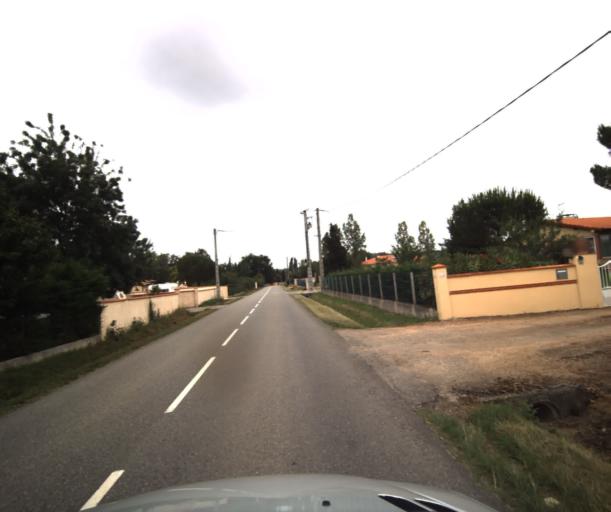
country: FR
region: Midi-Pyrenees
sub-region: Departement de la Haute-Garonne
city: Labarthe-sur-Leze
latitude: 43.4530
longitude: 1.4099
